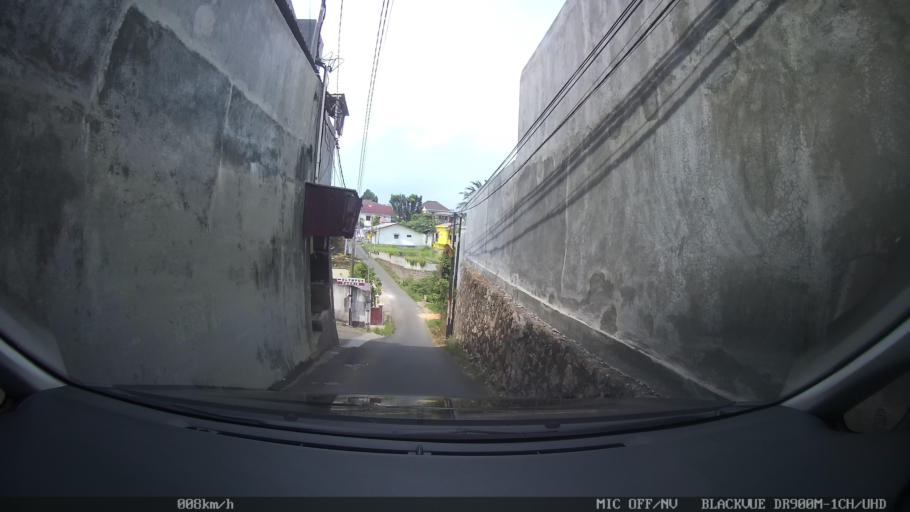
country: ID
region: Lampung
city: Bandarlampung
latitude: -5.4376
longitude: 105.2655
